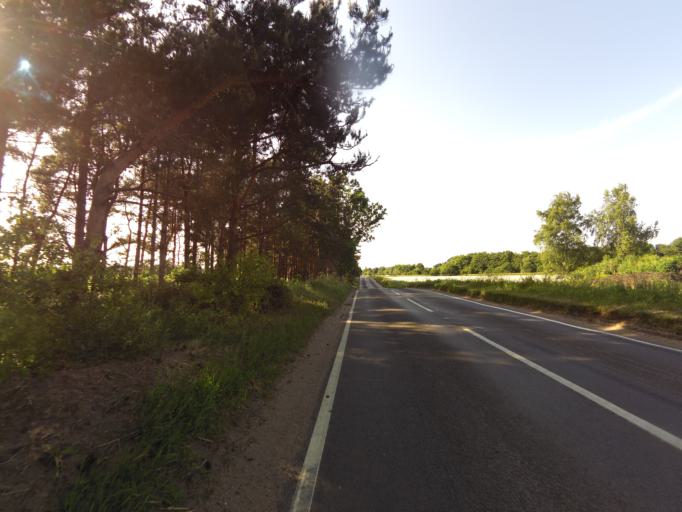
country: GB
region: England
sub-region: Suffolk
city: Woodbridge
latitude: 52.0894
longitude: 1.3547
